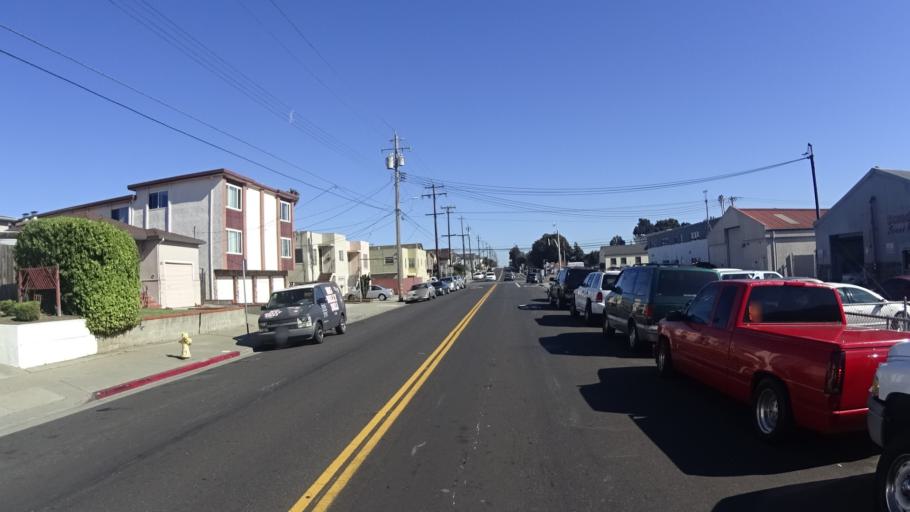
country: US
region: California
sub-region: San Mateo County
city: South San Francisco
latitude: 37.6539
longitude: -122.4181
